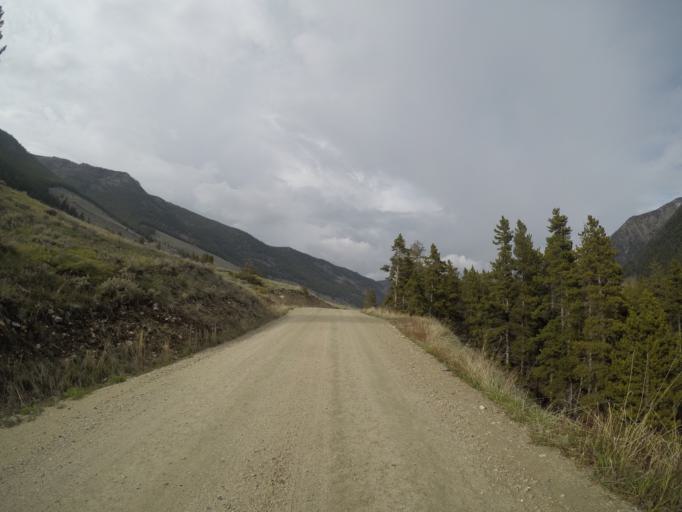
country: US
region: Montana
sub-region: Carbon County
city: Red Lodge
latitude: 45.0504
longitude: -109.4226
